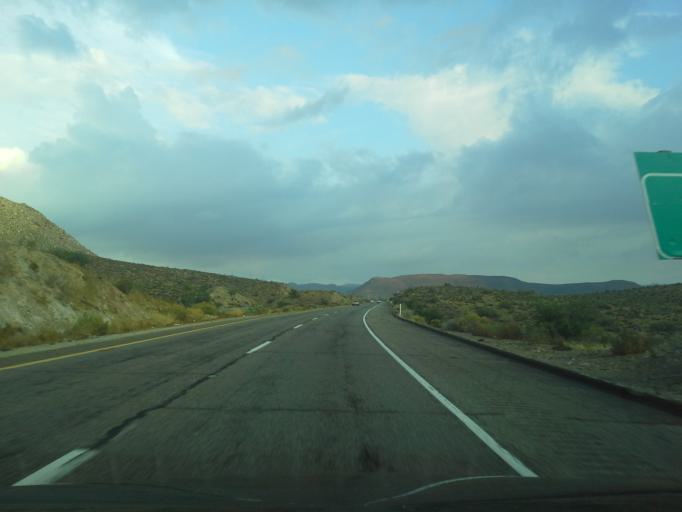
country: MX
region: Baja California
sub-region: Tecate
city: Cereso del Hongo
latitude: 32.6423
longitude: -116.1762
